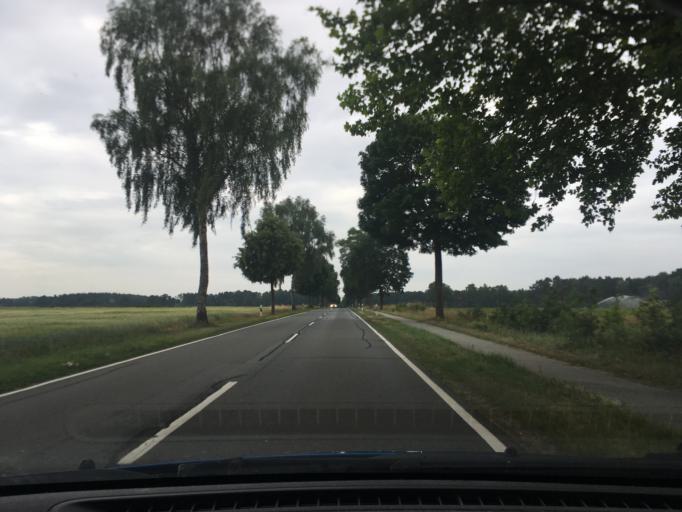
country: DE
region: Lower Saxony
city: Wenzendorf
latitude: 53.3454
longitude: 9.7554
